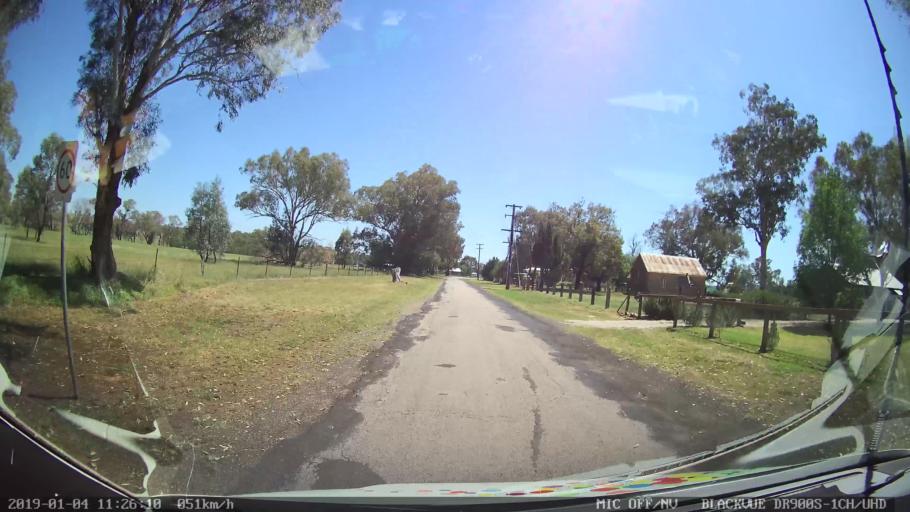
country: AU
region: New South Wales
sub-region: Cabonne
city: Molong
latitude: -33.1170
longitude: 148.7554
